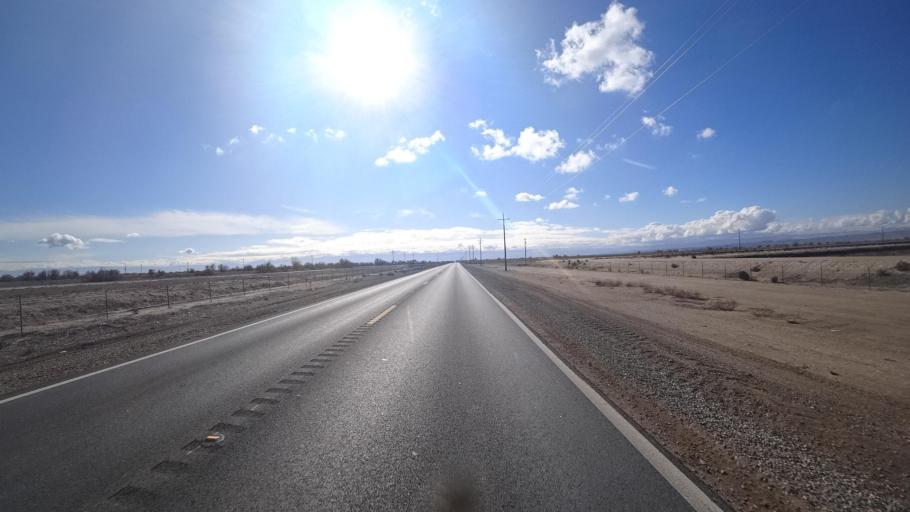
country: US
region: California
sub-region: Kern County
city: Rosedale
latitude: 35.3412
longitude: -119.2523
